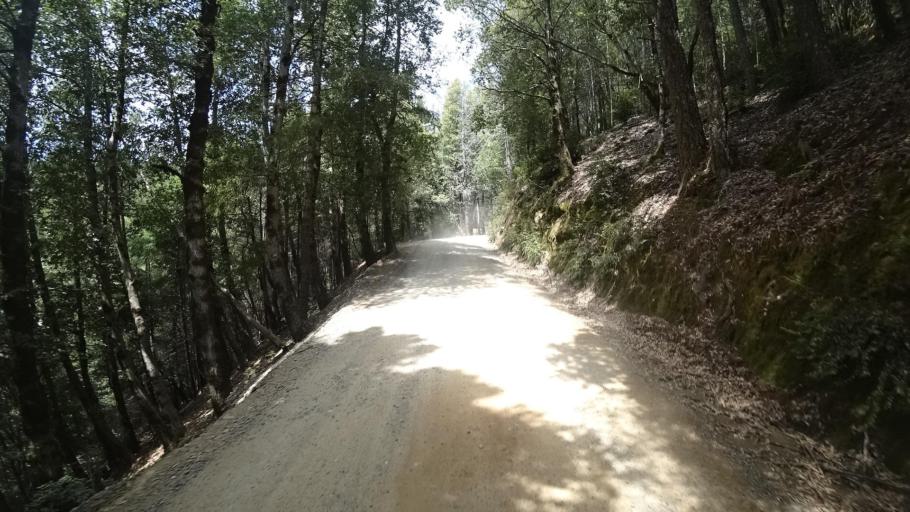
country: US
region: California
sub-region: Humboldt County
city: Redway
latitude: 40.0130
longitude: -123.9870
